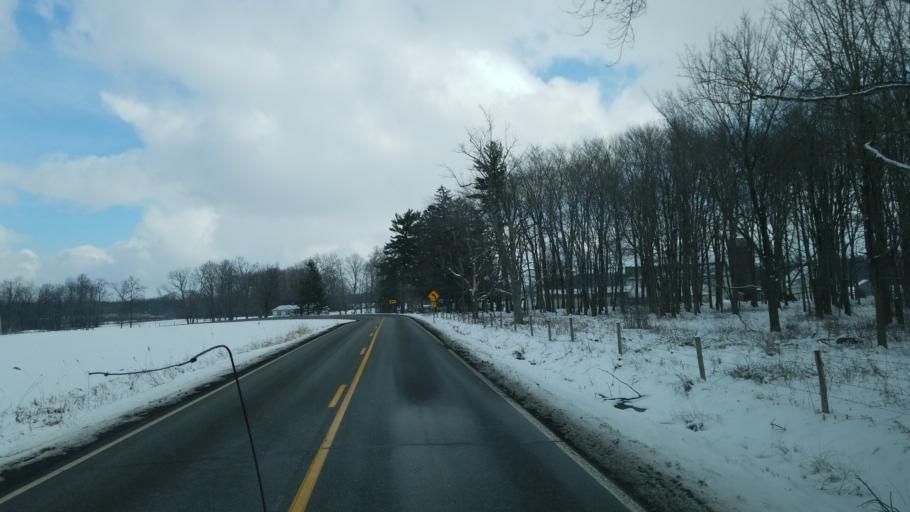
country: US
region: Ohio
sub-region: Geauga County
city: Burton
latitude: 41.4590
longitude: -81.1286
